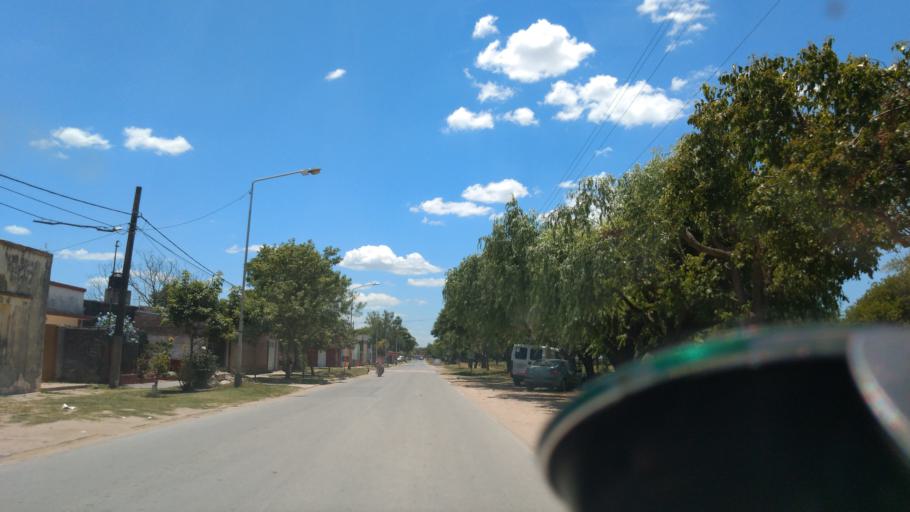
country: AR
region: Santa Fe
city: Laguna Paiva
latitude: -31.3125
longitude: -60.6584
